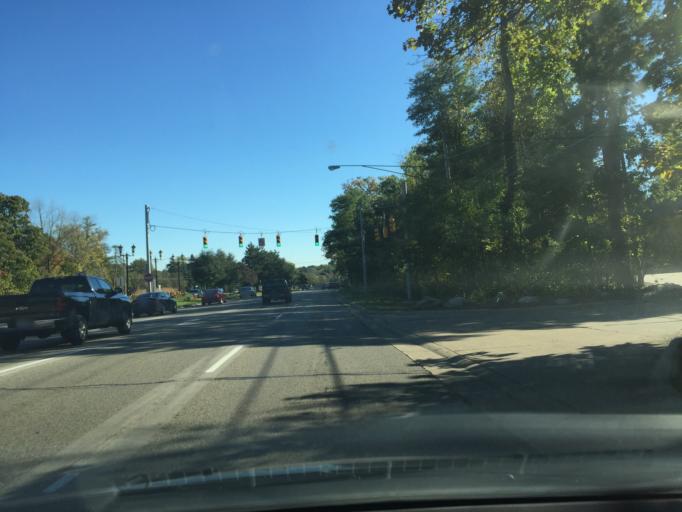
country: US
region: Michigan
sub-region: Oakland County
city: Bloomfield Hills
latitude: 42.5880
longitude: -83.2488
